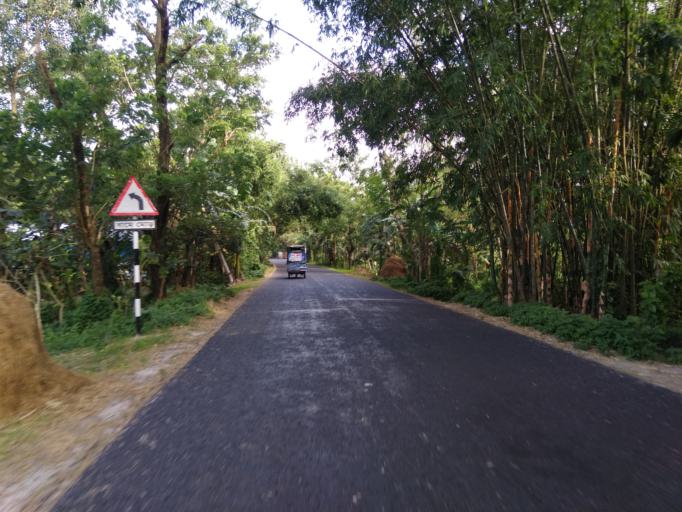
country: BD
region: Rangpur Division
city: Rangpur
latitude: 25.8385
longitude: 89.1140
